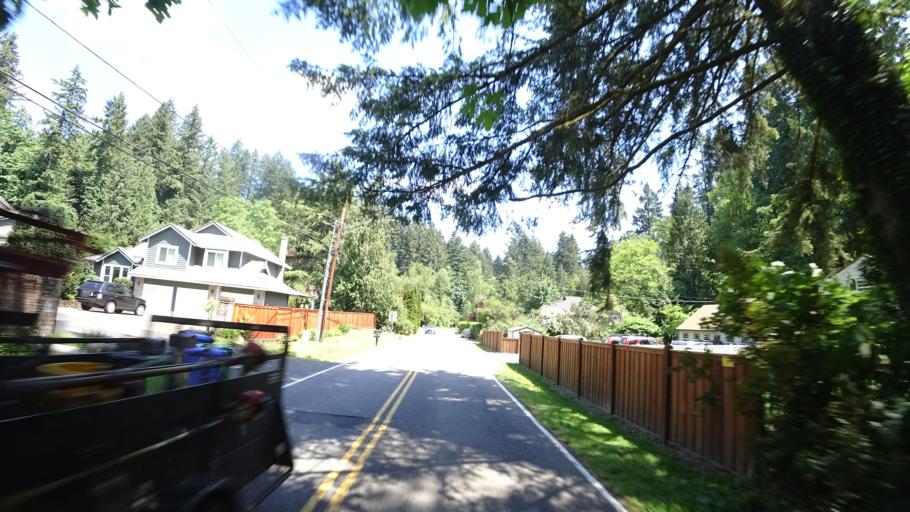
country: US
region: Oregon
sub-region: Clackamas County
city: Lake Oswego
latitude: 45.4466
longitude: -122.6992
